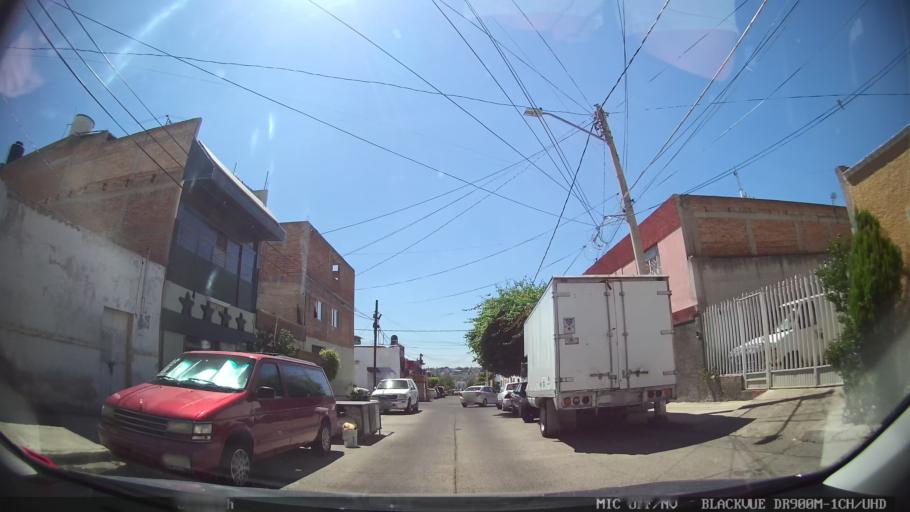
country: MX
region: Jalisco
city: Tlaquepaque
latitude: 20.6957
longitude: -103.2935
